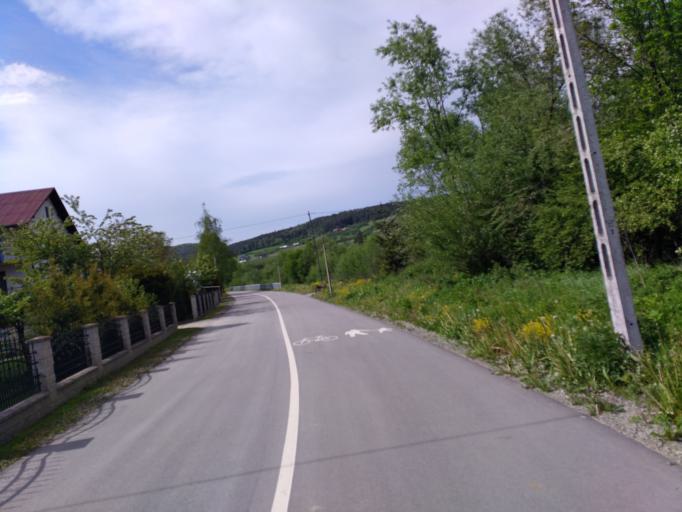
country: PL
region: Lesser Poland Voivodeship
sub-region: Powiat nowosadecki
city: Lacko
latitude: 49.5688
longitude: 20.4287
